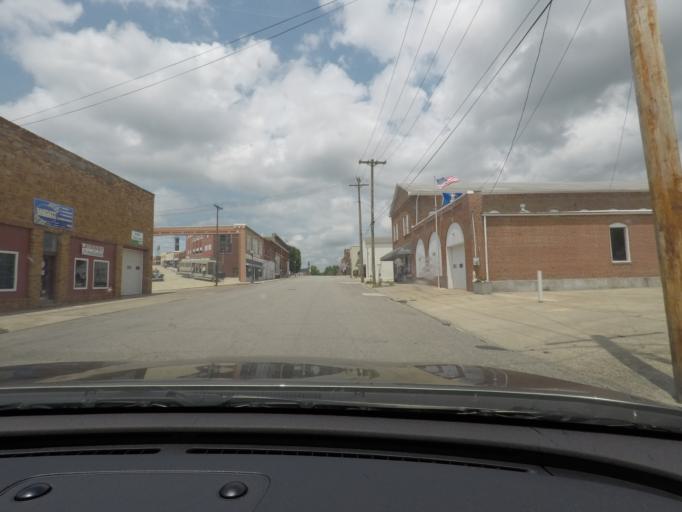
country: US
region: Missouri
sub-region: Carroll County
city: Carrollton
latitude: 39.3566
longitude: -93.4960
